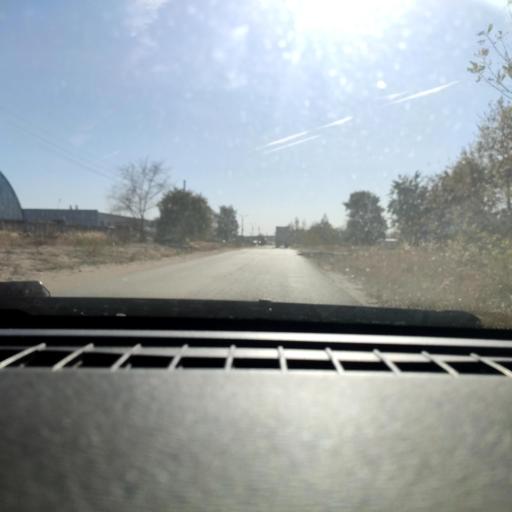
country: RU
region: Voronezj
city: Maslovka
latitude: 51.5933
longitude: 39.2369
